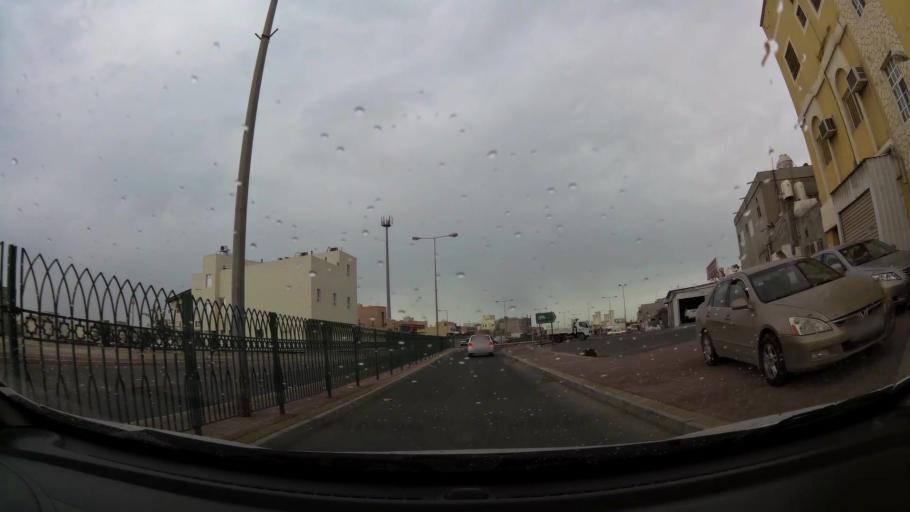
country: BH
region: Central Governorate
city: Madinat Hamad
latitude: 26.1172
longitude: 50.4798
